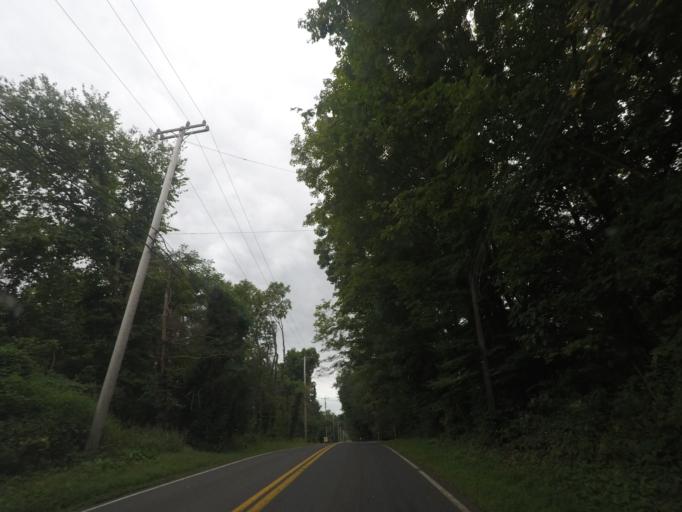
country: US
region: New York
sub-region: Rensselaer County
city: Nassau
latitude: 42.4660
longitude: -73.5798
